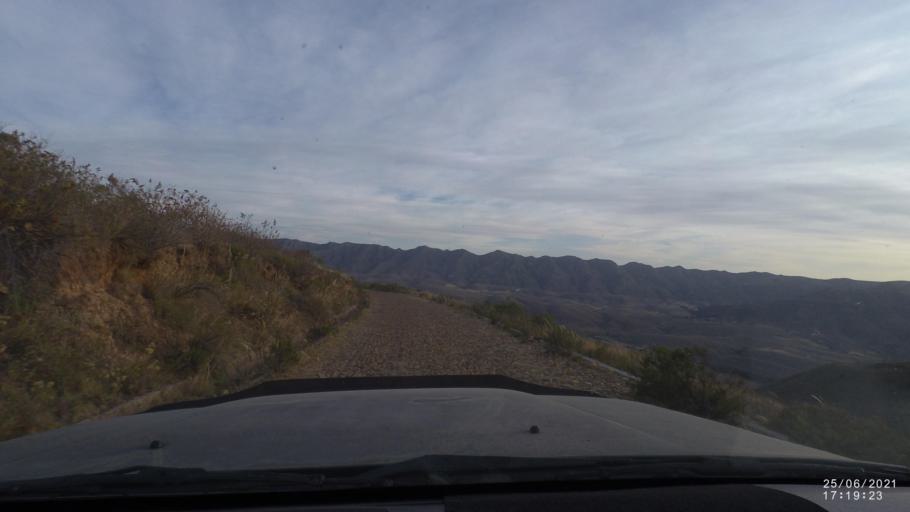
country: BO
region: Cochabamba
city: Arani
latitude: -17.9020
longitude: -65.6930
